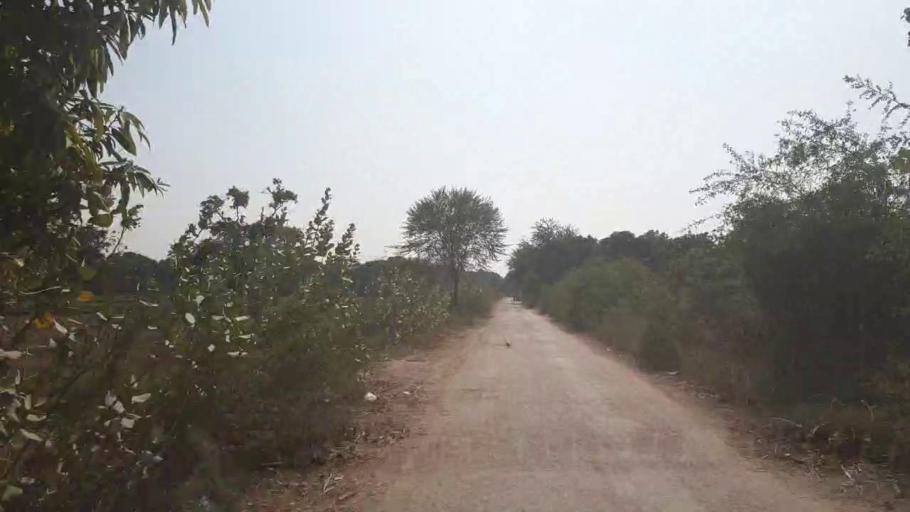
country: PK
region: Sindh
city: Tando Allahyar
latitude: 25.4848
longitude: 68.8480
